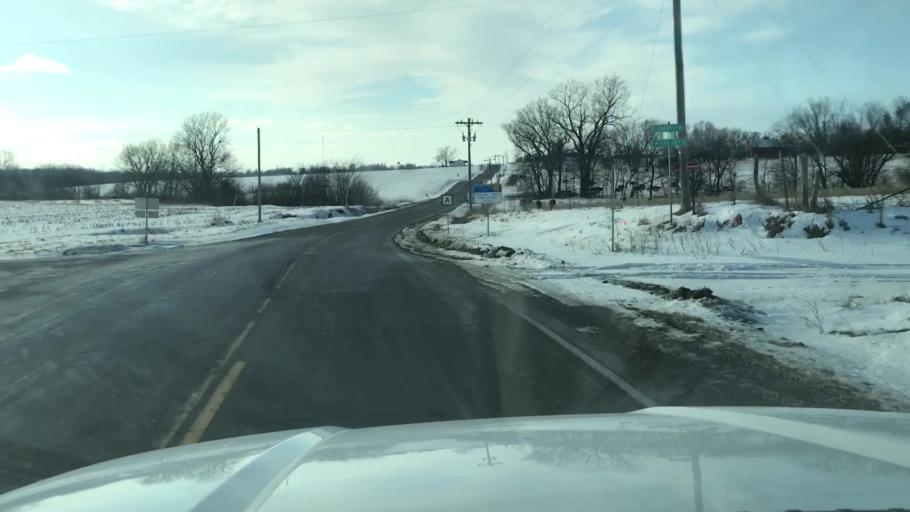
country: US
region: Missouri
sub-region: Nodaway County
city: Maryville
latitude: 40.2025
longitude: -95.0117
